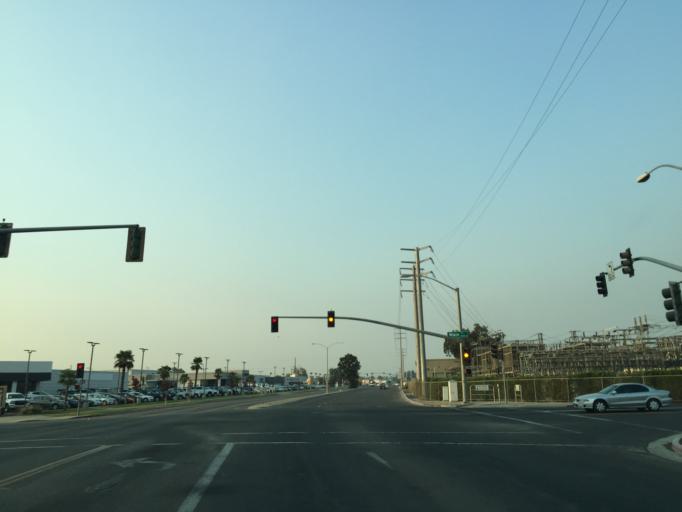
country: US
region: California
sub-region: Tulare County
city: Visalia
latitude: 36.3307
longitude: -119.2787
